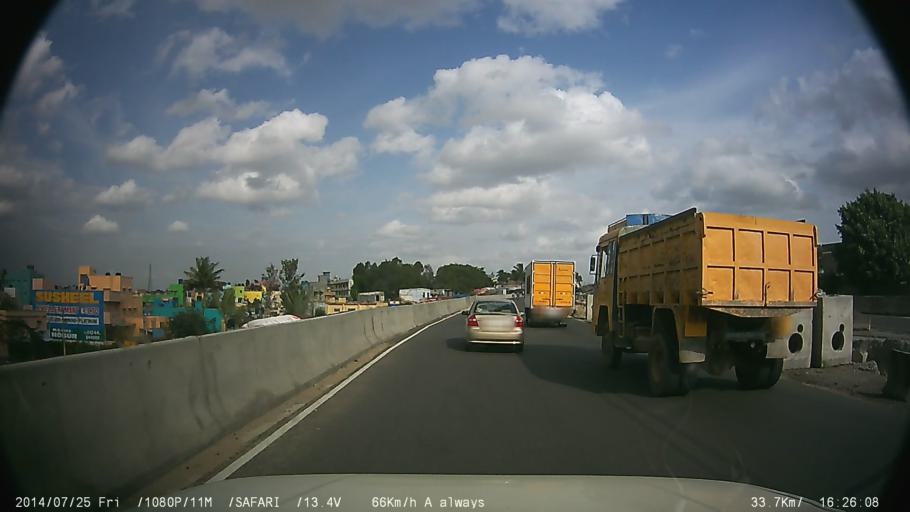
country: IN
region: Tamil Nadu
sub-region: Krishnagiri
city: Hosur
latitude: 12.7706
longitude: 77.7865
